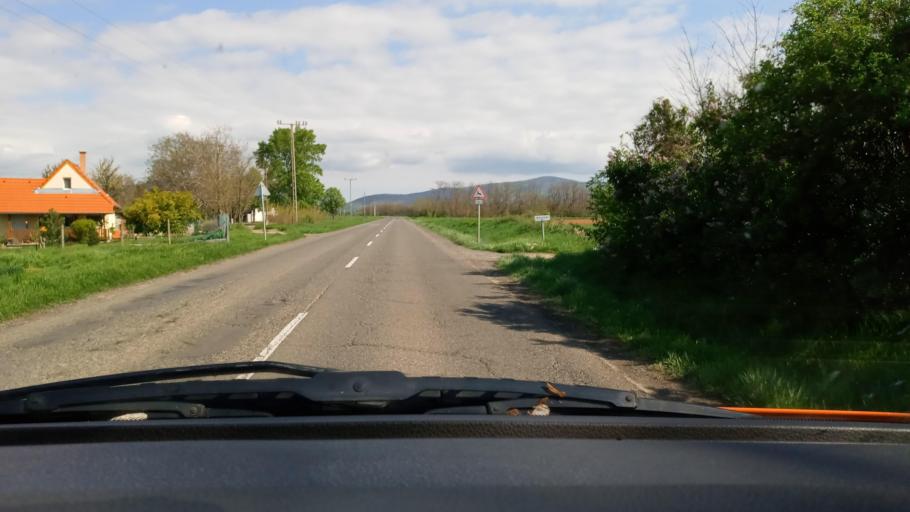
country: HU
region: Baranya
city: Hosszuheteny
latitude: 46.1184
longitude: 18.3480
